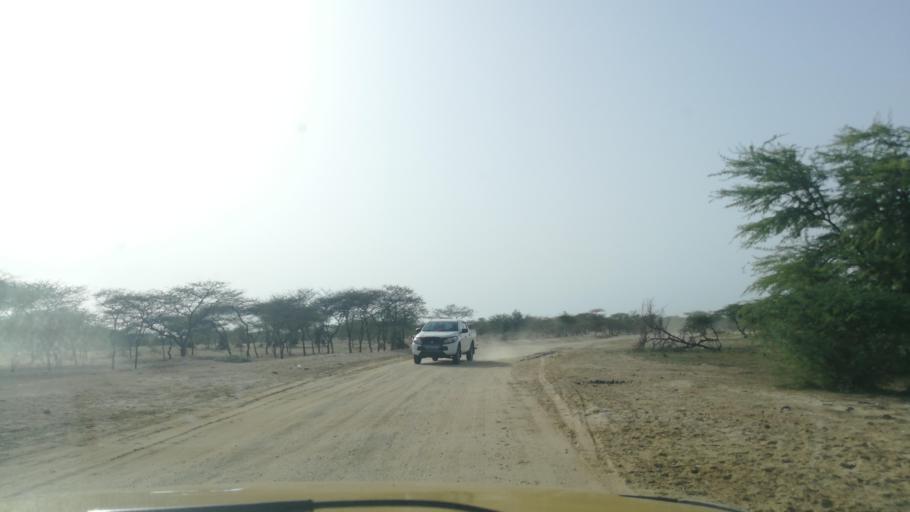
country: SN
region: Saint-Louis
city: Saint-Louis
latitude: 16.0598
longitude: -16.3331
